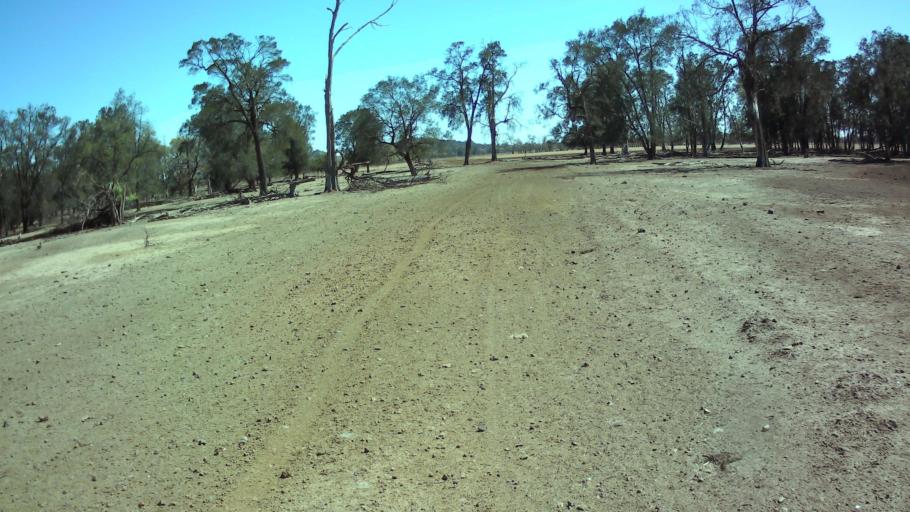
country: AU
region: New South Wales
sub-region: Bland
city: West Wyalong
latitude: -33.7574
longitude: 147.6592
